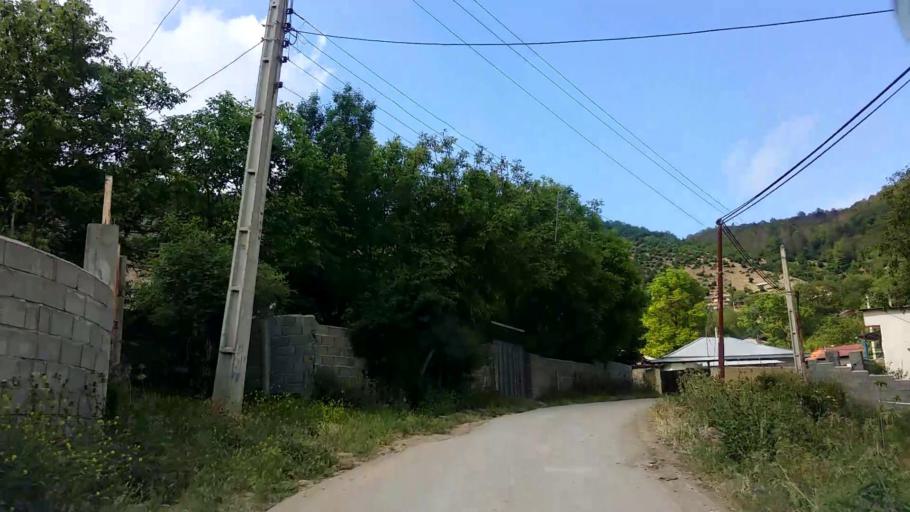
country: IR
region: Mazandaran
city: Chalus
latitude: 36.5564
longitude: 51.2893
